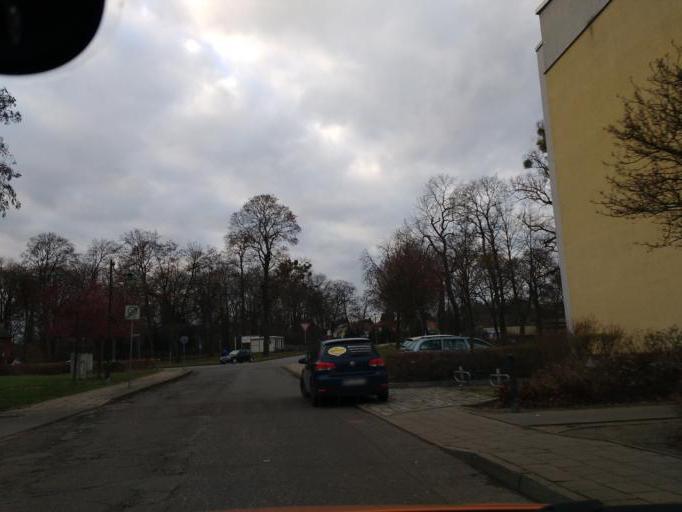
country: DE
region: Brandenburg
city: Wriezen
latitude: 52.7180
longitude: 14.1326
